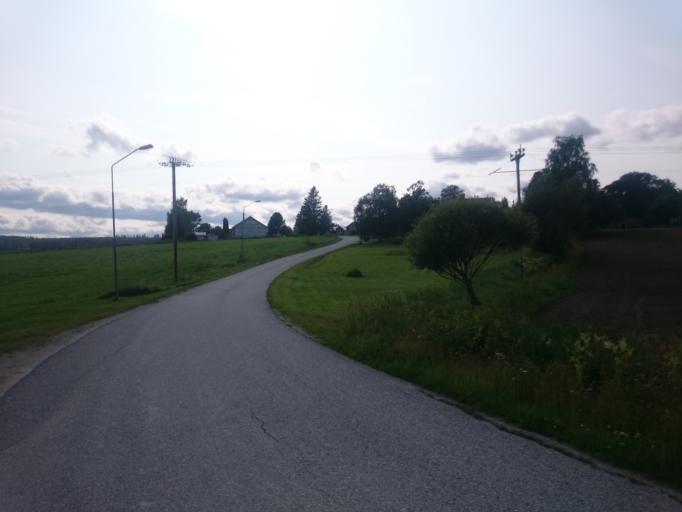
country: SE
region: Vaesternorrland
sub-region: OErnskoeldsviks Kommun
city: Bredbyn
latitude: 63.3010
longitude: 18.2767
